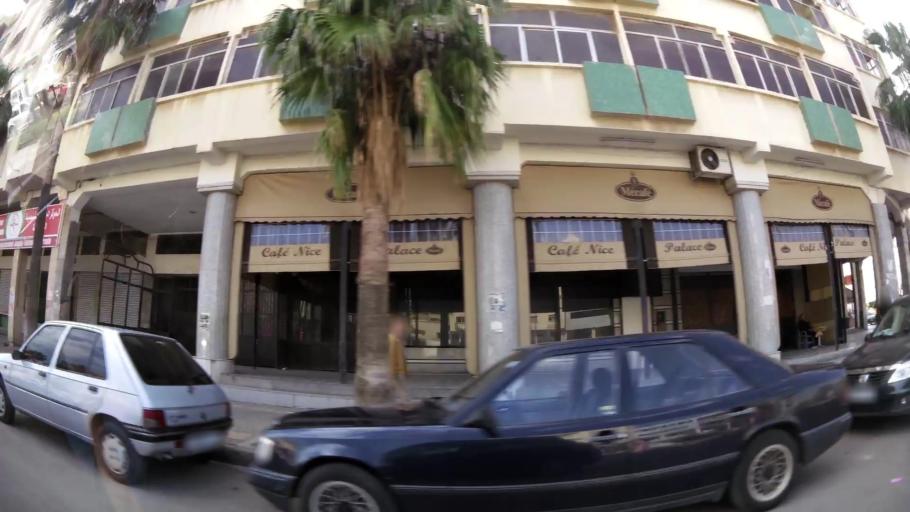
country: MA
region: Oriental
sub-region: Oujda-Angad
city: Oujda
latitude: 34.6848
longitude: -1.9144
